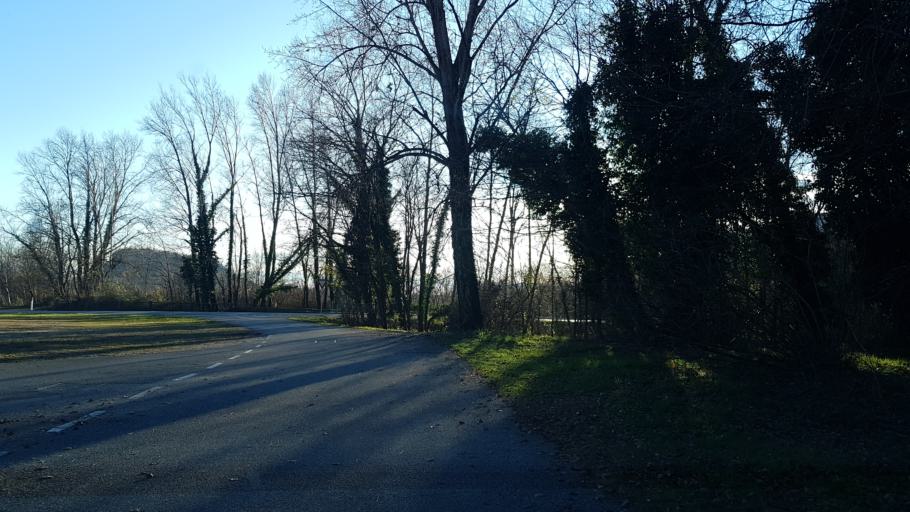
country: IT
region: Friuli Venezia Giulia
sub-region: Provincia di Udine
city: Trasaghis
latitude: 46.2826
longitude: 13.0857
